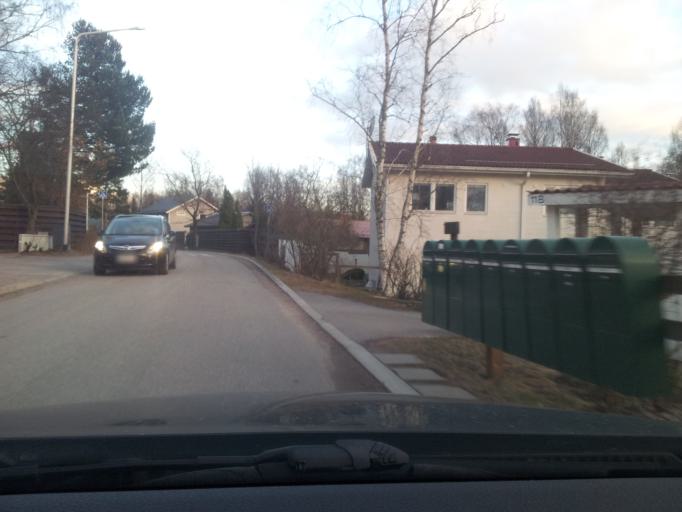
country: FI
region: Uusimaa
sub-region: Helsinki
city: Koukkuniemi
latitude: 60.1730
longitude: 24.7709
